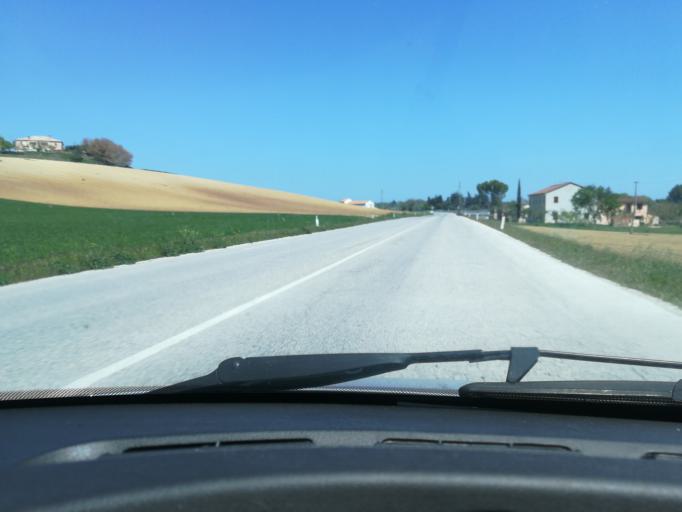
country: IT
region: The Marches
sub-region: Provincia di Ancona
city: Villa Musone
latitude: 43.4627
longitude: 13.5994
